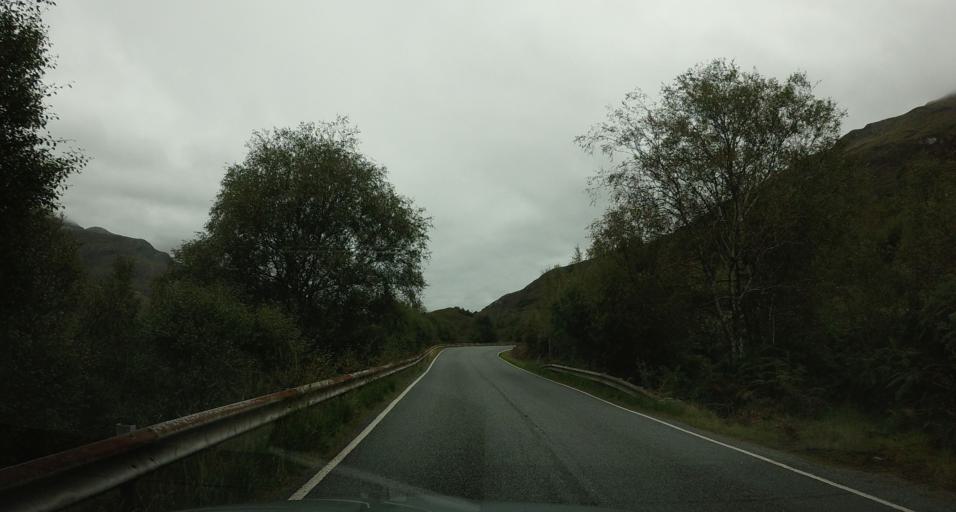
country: GB
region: Scotland
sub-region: Highland
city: Fort William
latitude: 56.7069
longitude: -5.0127
